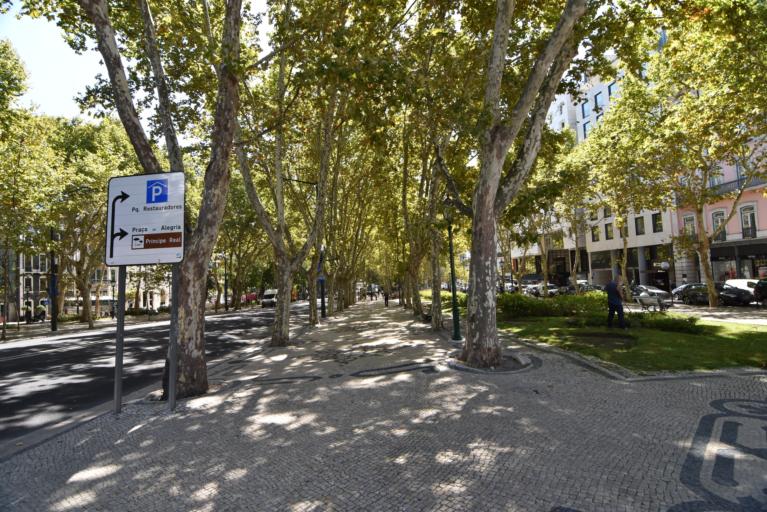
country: PT
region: Lisbon
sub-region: Lisbon
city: Lisbon
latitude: 38.7194
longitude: -9.1450
